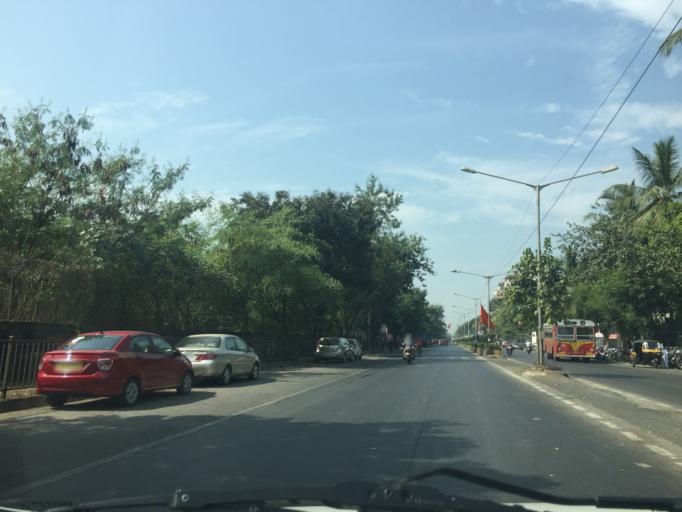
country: IN
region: Maharashtra
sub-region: Mumbai Suburban
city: Borivli
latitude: 19.2320
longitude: 72.8311
